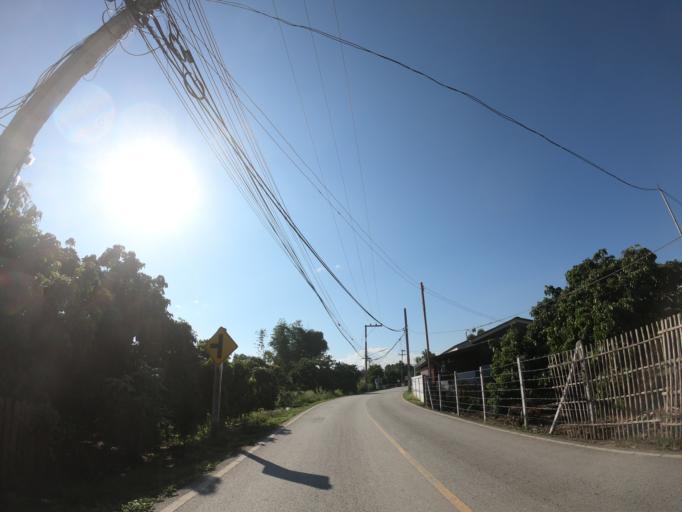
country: TH
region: Chiang Mai
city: Saraphi
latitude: 18.6999
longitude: 98.9898
